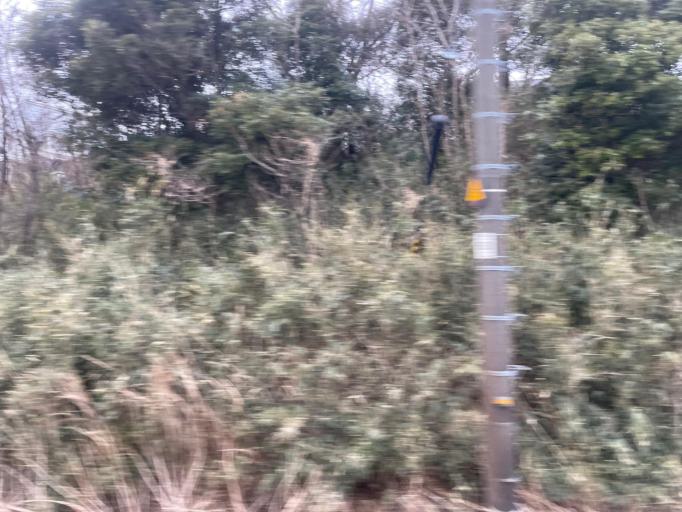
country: JP
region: Gunma
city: Kanekomachi
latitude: 36.4446
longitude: 139.0233
